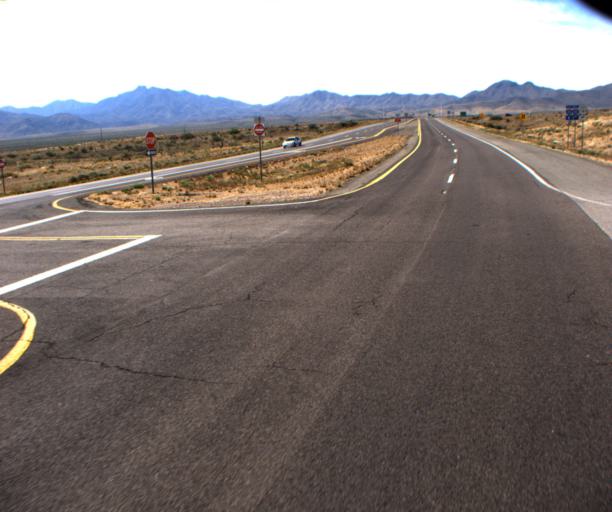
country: US
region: Arizona
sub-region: Cochise County
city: Willcox
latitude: 32.3630
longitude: -109.6814
